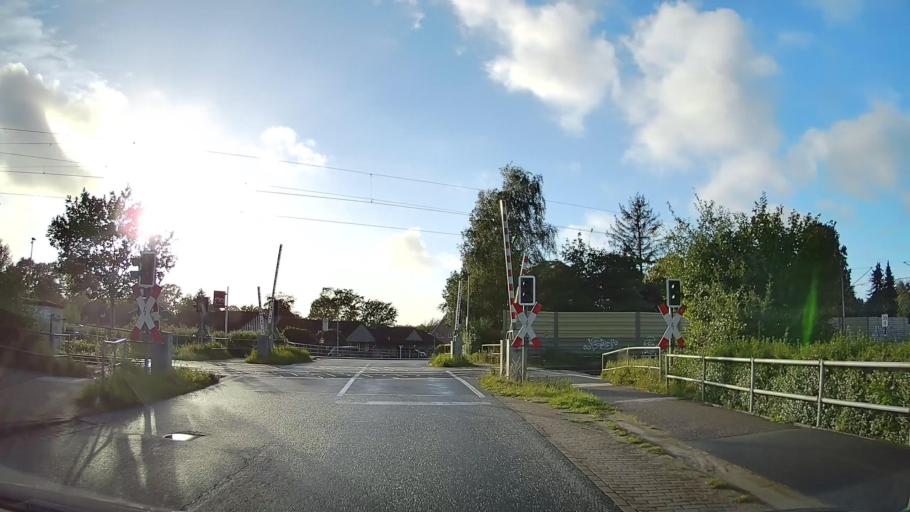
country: DE
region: Schleswig-Holstein
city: Horst
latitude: 53.8055
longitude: 9.6452
